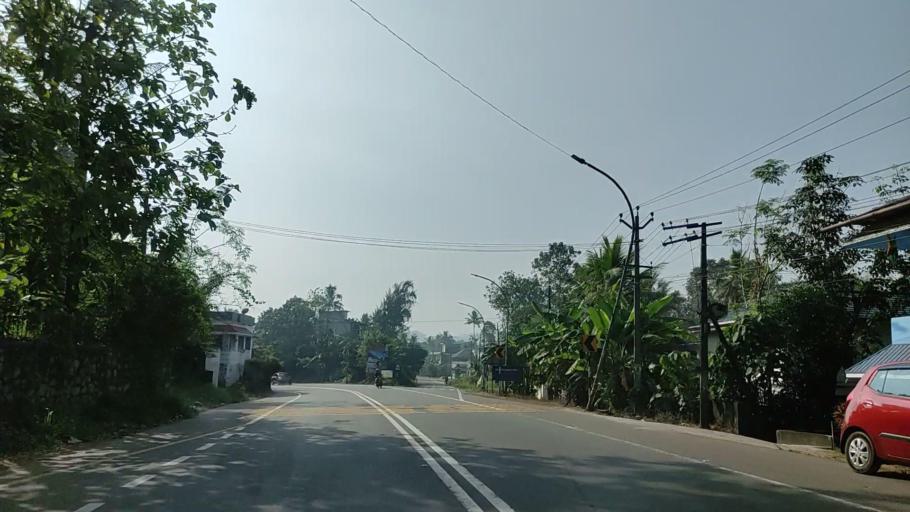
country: IN
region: Kerala
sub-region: Kollam
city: Punalur
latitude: 8.9807
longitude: 76.8103
